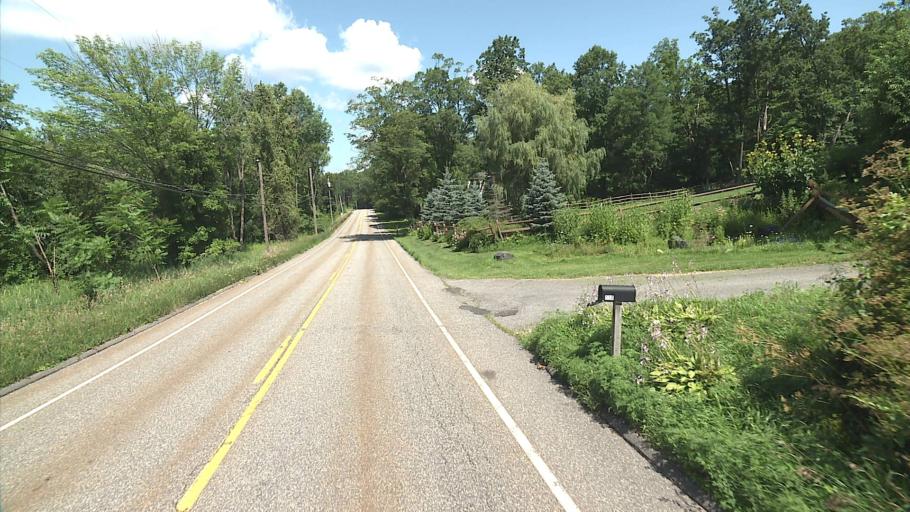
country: US
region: Connecticut
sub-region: Litchfield County
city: New Preston
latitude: 41.7950
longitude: -73.3682
